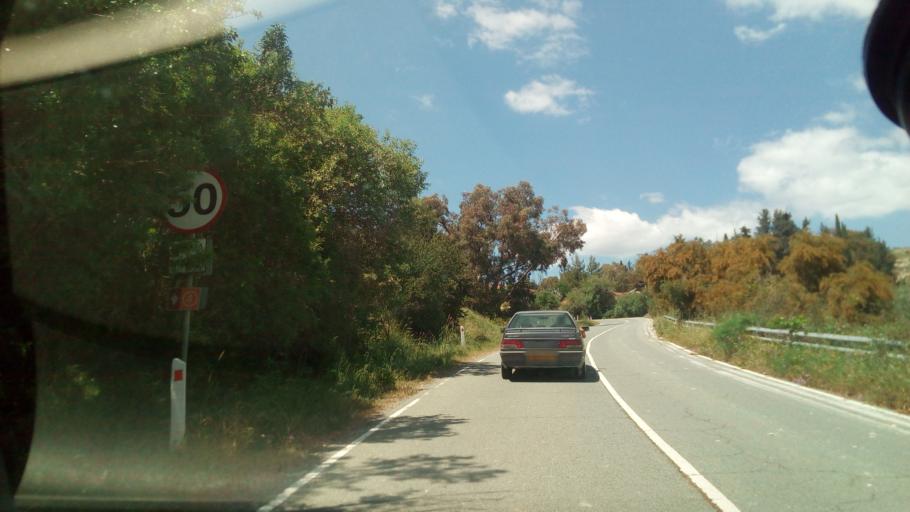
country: CY
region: Limassol
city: Pachna
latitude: 34.8146
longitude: 32.7866
